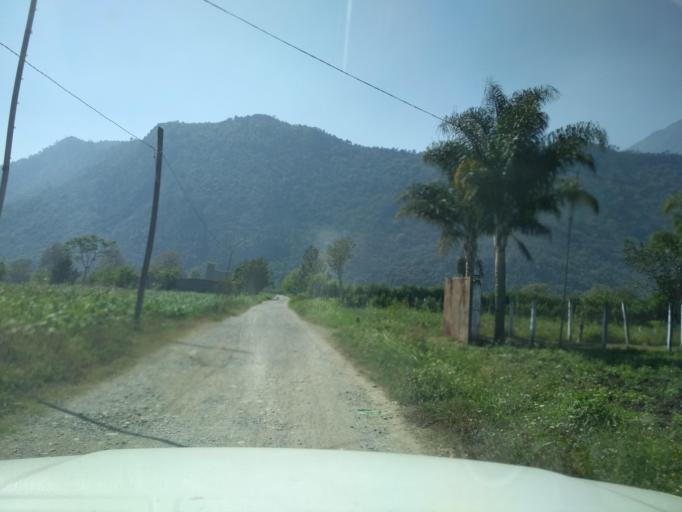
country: MX
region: Veracruz
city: Jalapilla
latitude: 18.8133
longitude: -97.0862
